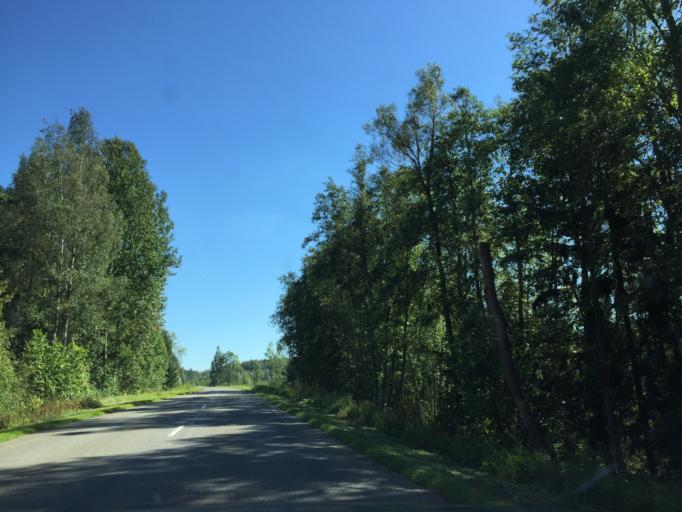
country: LV
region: Akniste
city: Akniste
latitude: 56.0804
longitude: 25.8791
